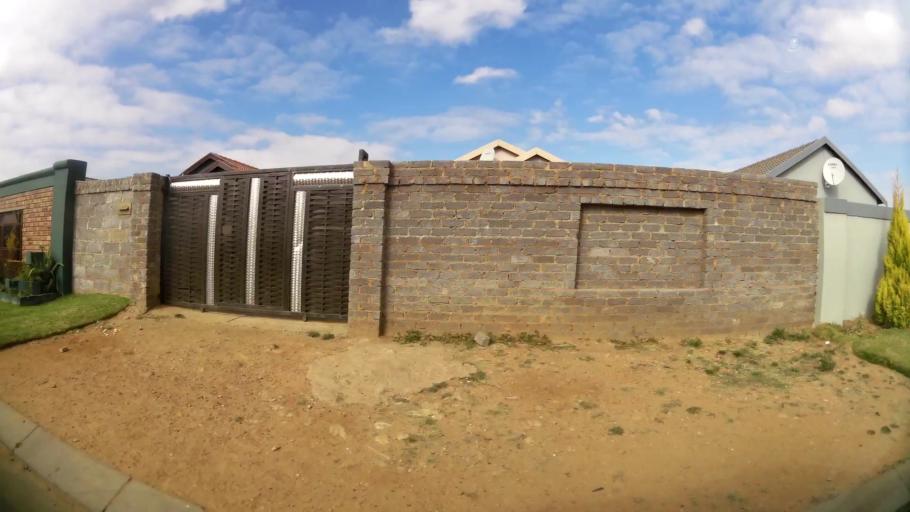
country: ZA
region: Gauteng
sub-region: City of Johannesburg Metropolitan Municipality
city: Roodepoort
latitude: -26.2048
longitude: 27.9138
